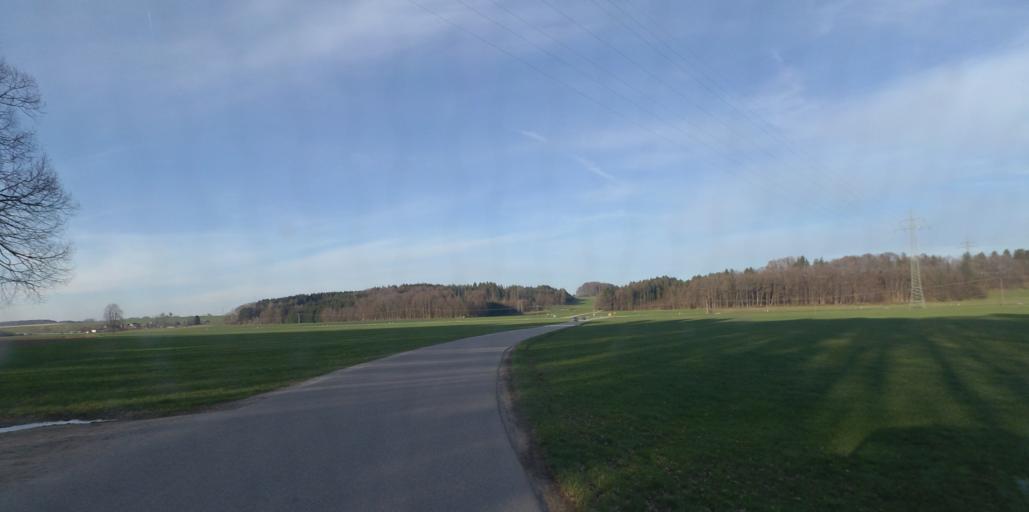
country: DE
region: Bavaria
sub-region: Upper Bavaria
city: Vachendorf
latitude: 47.8536
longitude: 12.5897
